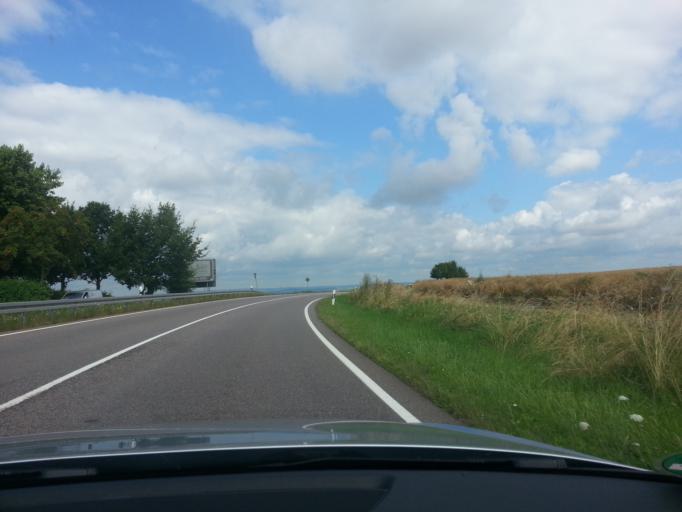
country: DE
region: Rheinland-Pfalz
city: Kirf
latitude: 49.5180
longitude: 6.4469
